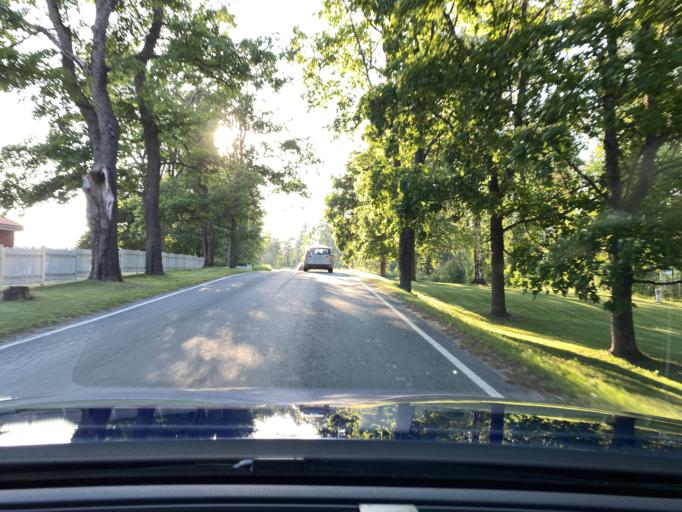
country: FI
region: Haeme
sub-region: Haemeenlinna
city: Tervakoski
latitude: 60.7406
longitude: 24.6551
